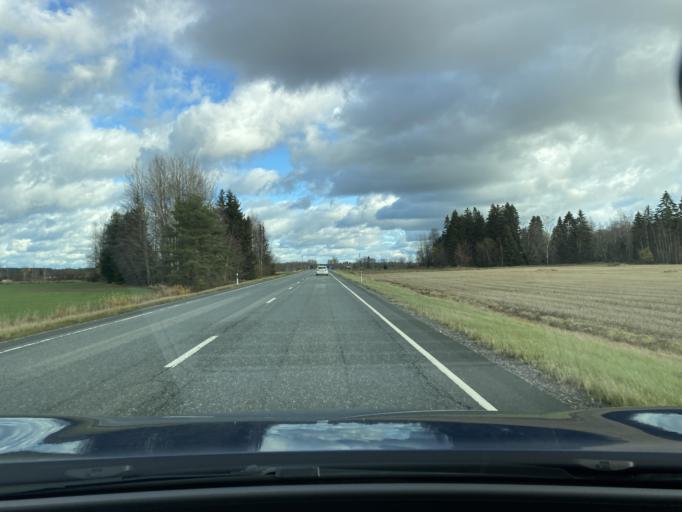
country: FI
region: Haeme
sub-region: Forssa
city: Humppila
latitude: 60.9495
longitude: 23.3224
